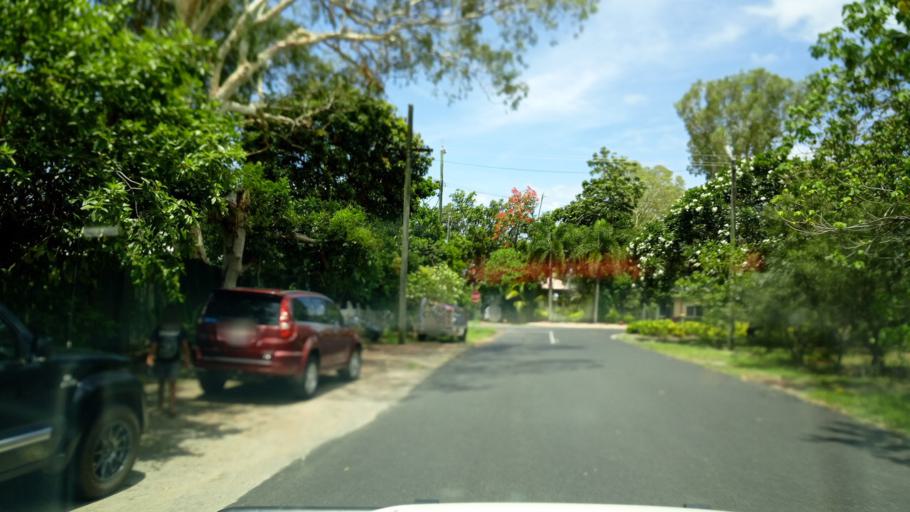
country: AU
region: Queensland
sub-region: Cairns
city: Yorkeys Knob
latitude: -16.8506
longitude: 145.7473
